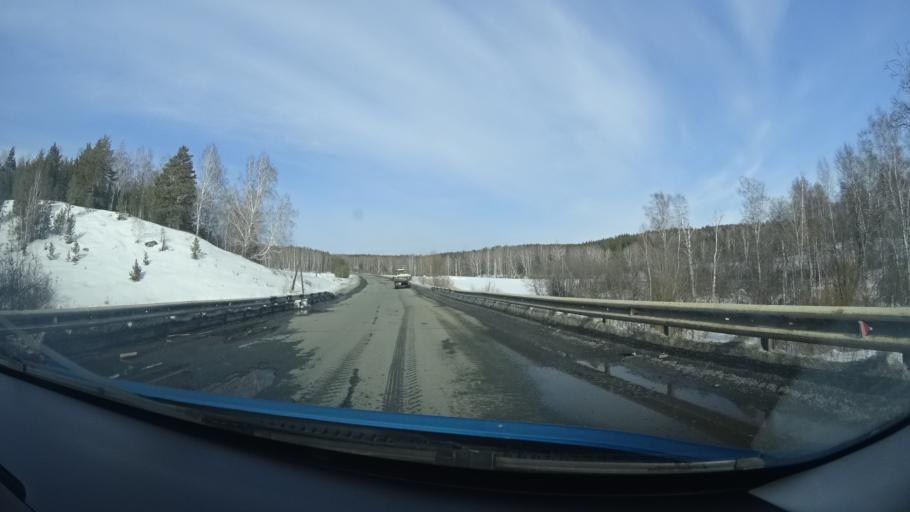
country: RU
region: Bashkortostan
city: Lomovka
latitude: 53.8195
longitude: 58.2772
